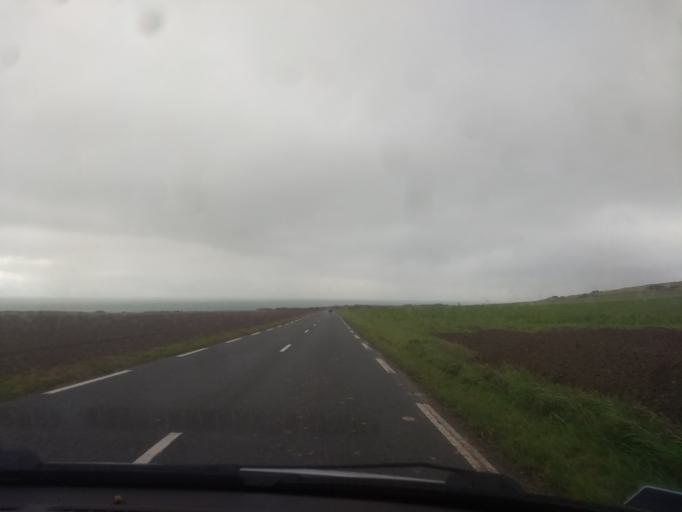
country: FR
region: Nord-Pas-de-Calais
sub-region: Departement du Pas-de-Calais
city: Sangatte
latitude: 50.9340
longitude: 1.7248
